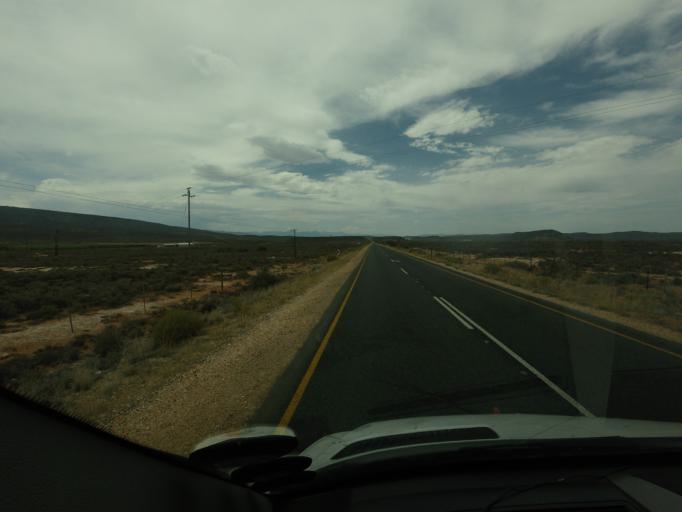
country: ZA
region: Western Cape
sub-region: Overberg District Municipality
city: Swellendam
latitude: -33.8415
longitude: 20.8679
